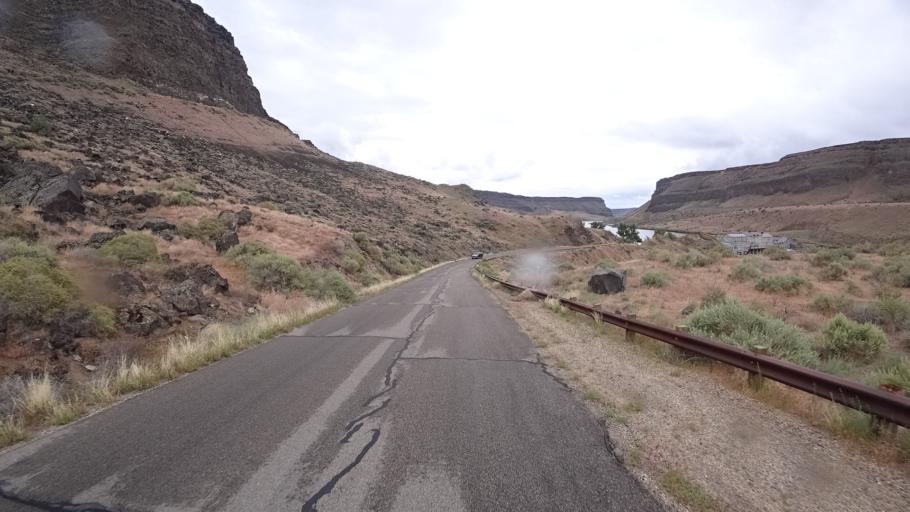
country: US
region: Idaho
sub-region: Owyhee County
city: Murphy
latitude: 43.2475
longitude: -116.3763
